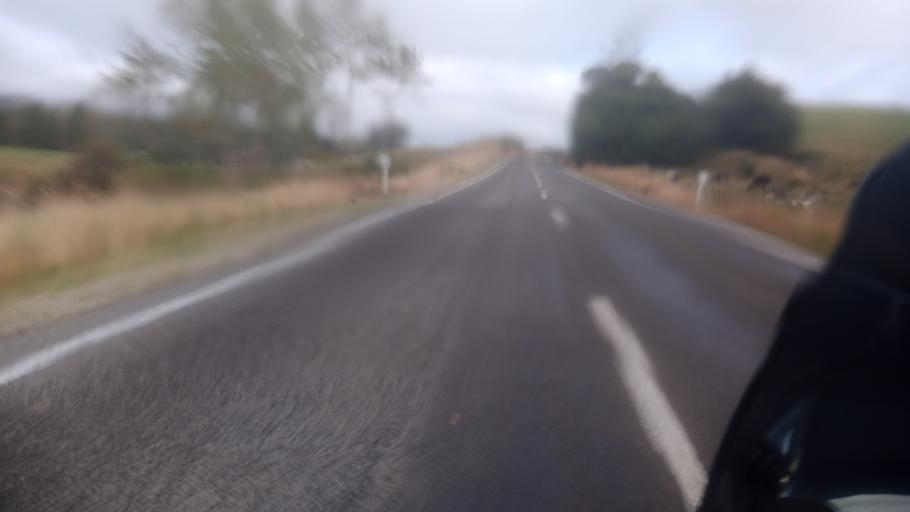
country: NZ
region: Bay of Plenty
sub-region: Opotiki District
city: Opotiki
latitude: -38.3806
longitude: 177.5522
